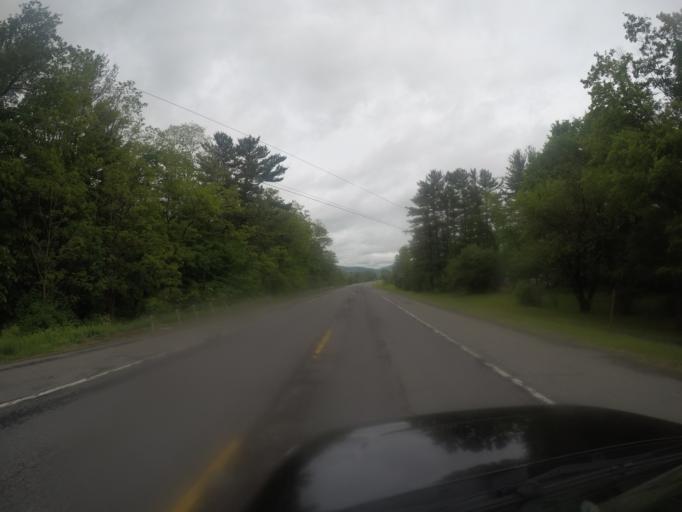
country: US
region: New York
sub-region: Ulster County
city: Shokan
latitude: 42.0426
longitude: -74.2821
